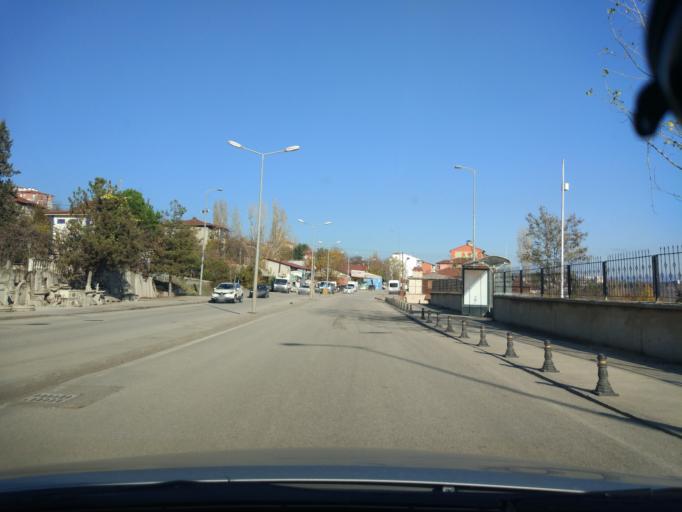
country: TR
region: Karabuk
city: Karabuk
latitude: 41.2057
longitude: 32.6338
